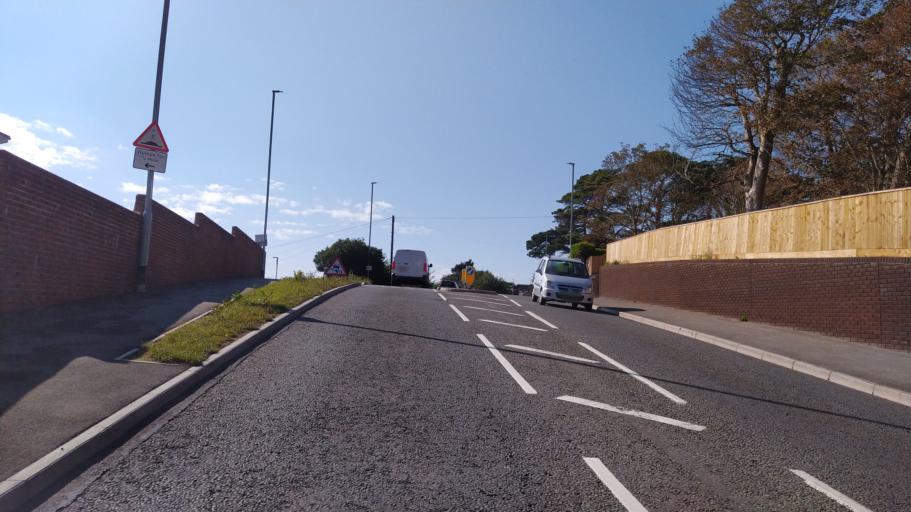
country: GB
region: England
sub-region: Dorset
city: Weymouth
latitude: 50.5986
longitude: -2.4710
